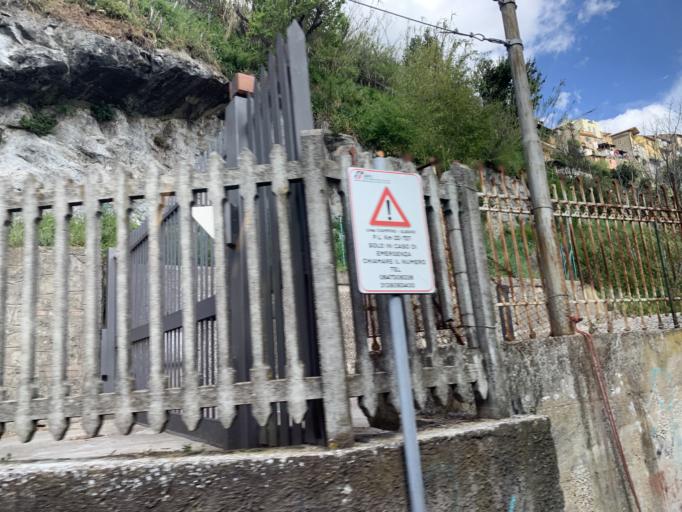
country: IT
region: Latium
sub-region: Citta metropolitana di Roma Capitale
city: Castel Gandolfo
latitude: 41.7680
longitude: 12.6590
